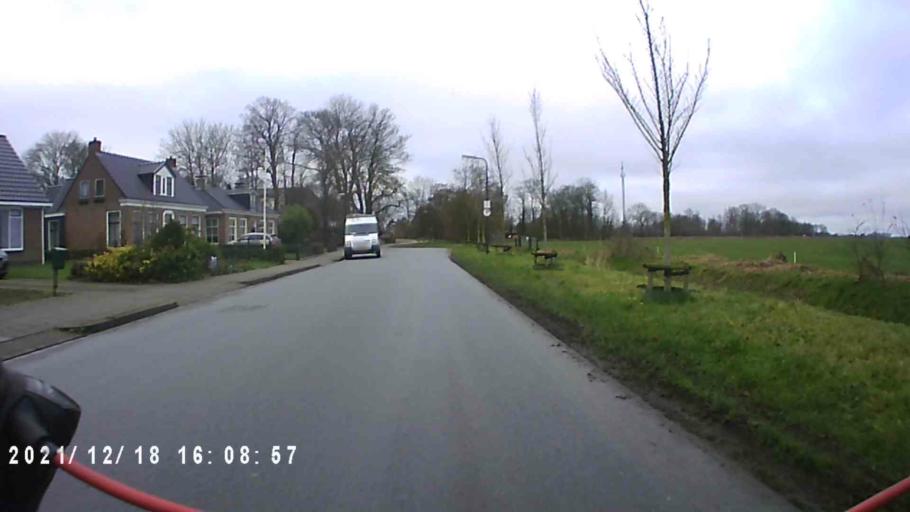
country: NL
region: Friesland
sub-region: Gemeente Dongeradeel
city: Anjum
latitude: 53.3599
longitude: 6.0723
